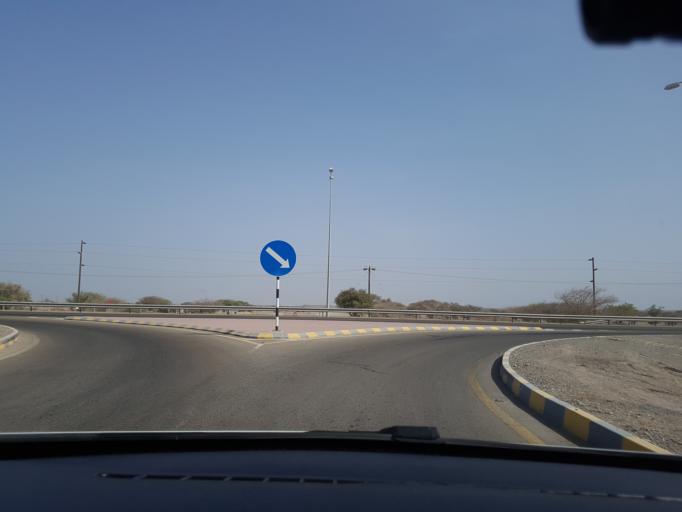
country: OM
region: Al Batinah
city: Al Liwa'
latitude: 24.4023
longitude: 56.5821
